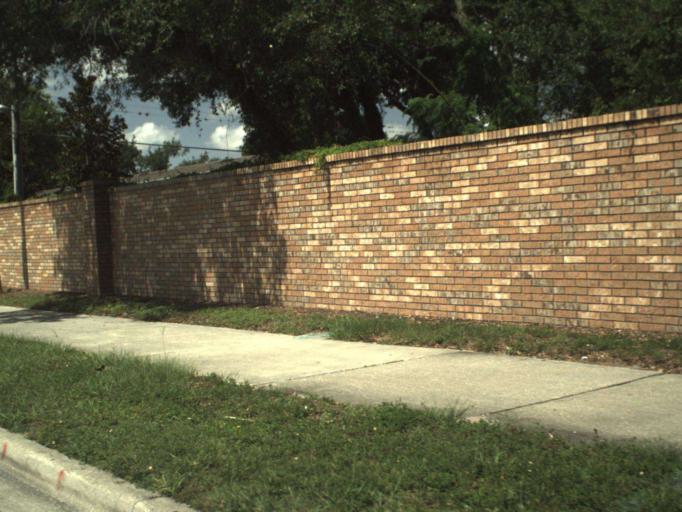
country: US
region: Florida
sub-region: Orange County
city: Conway
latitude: 28.4845
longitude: -81.3309
